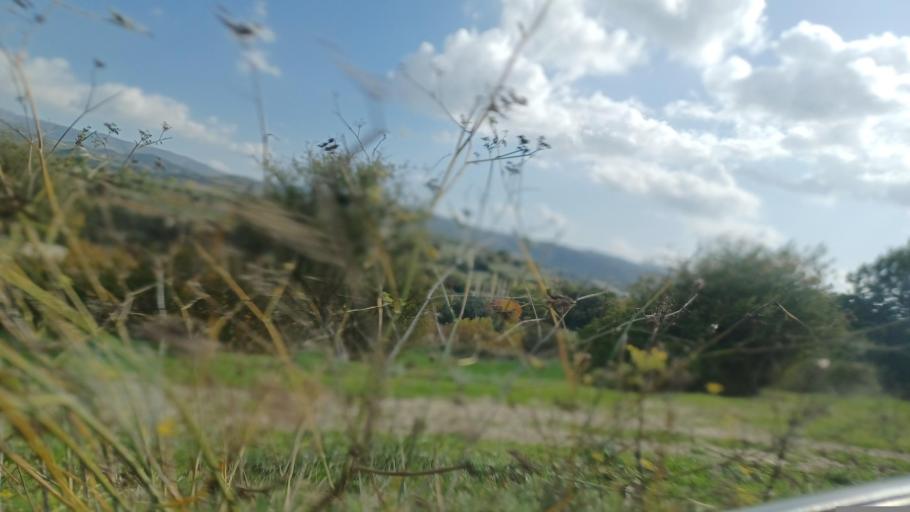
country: CY
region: Pafos
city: Mesogi
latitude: 34.8622
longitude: 32.5374
